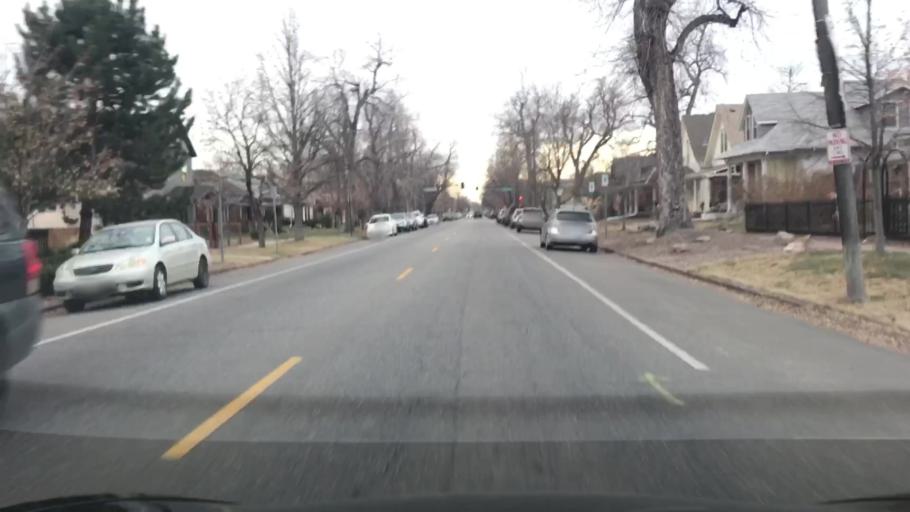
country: US
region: Colorado
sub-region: Denver County
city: Denver
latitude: 39.7034
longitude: -104.9828
